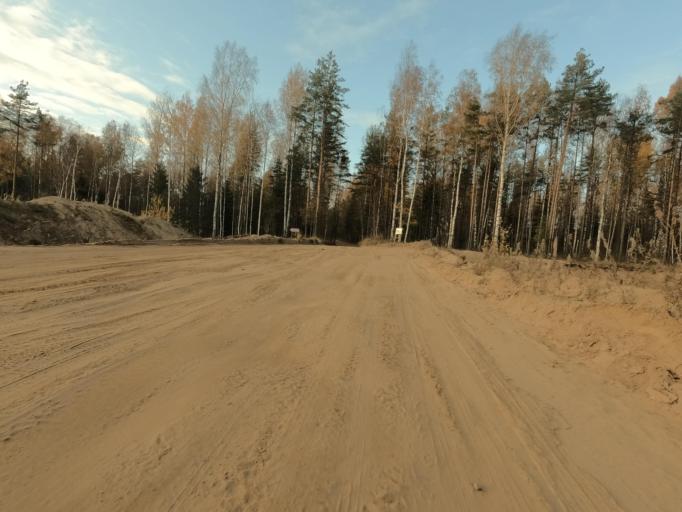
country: RU
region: Leningrad
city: Priladozhskiy
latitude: 59.7391
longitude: 31.3165
